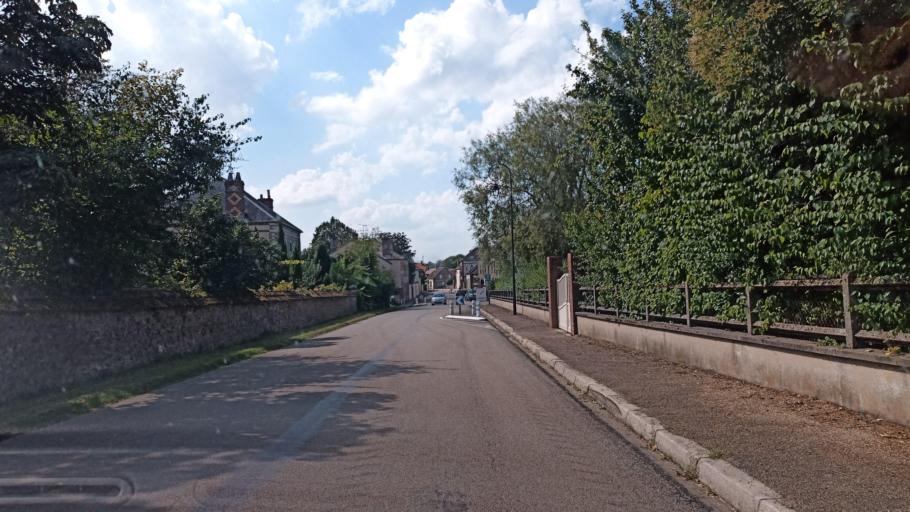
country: FR
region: Bourgogne
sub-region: Departement de l'Yonne
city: Egriselles-le-Bocage
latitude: 48.0547
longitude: 3.1497
